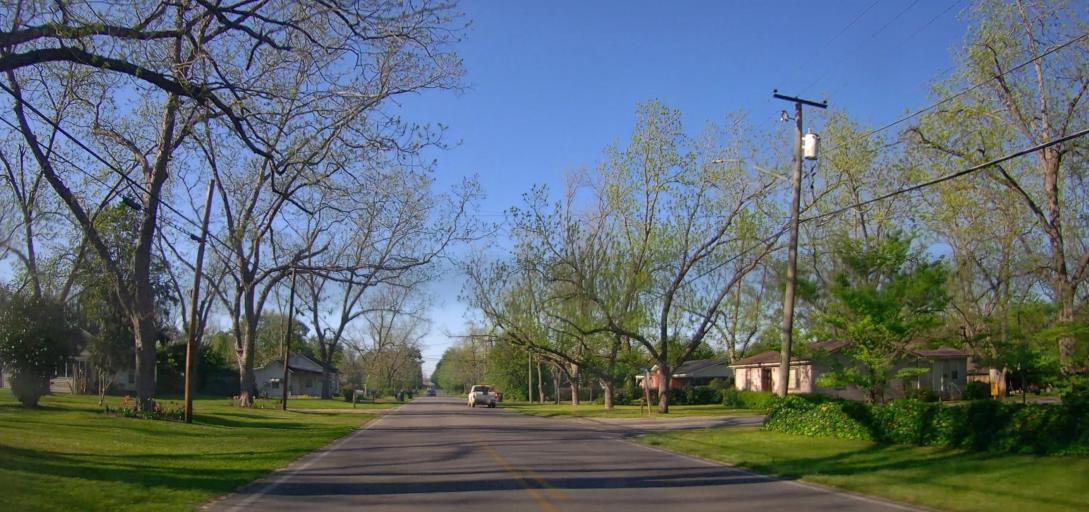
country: US
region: Georgia
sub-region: Ben Hill County
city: Fitzgerald
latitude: 31.7261
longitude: -83.2652
